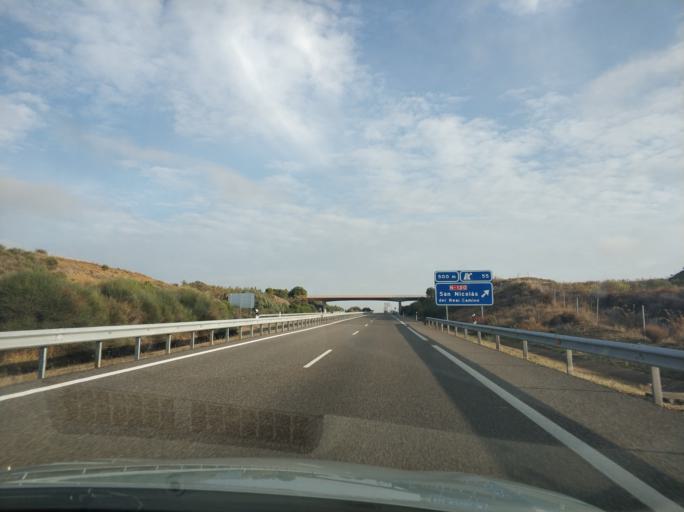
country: ES
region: Castille and Leon
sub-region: Provincia de Leon
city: Sahagun
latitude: 42.3706
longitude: -4.9881
